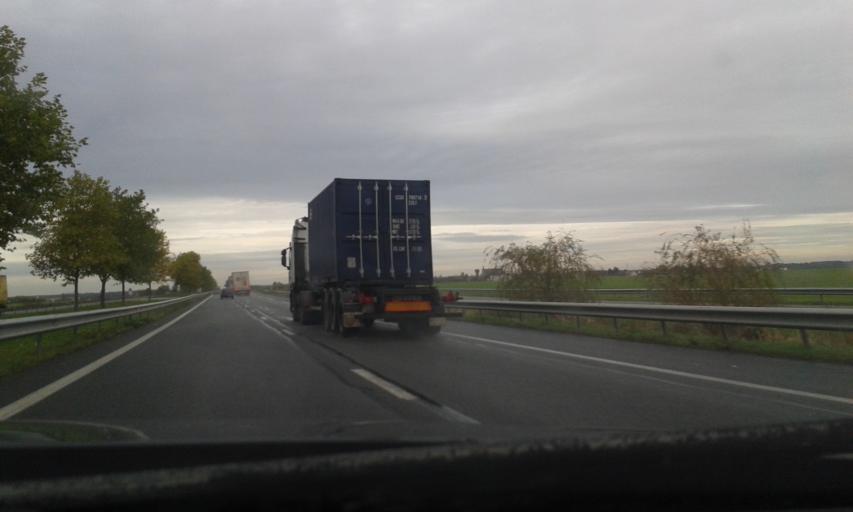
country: FR
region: Centre
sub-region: Departement d'Eure-et-Loir
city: Luray
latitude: 48.6653
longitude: 1.3915
